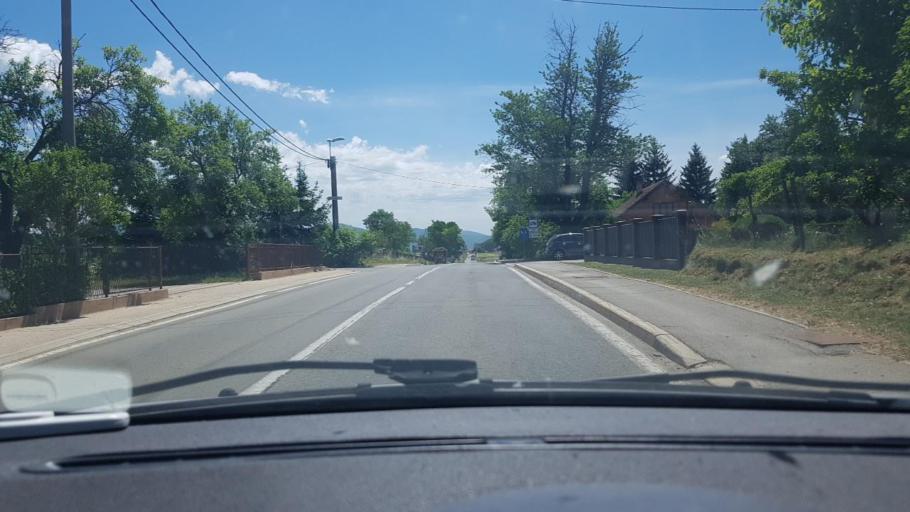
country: HR
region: Licko-Senjska
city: Otocac
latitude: 44.8619
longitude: 15.2629
